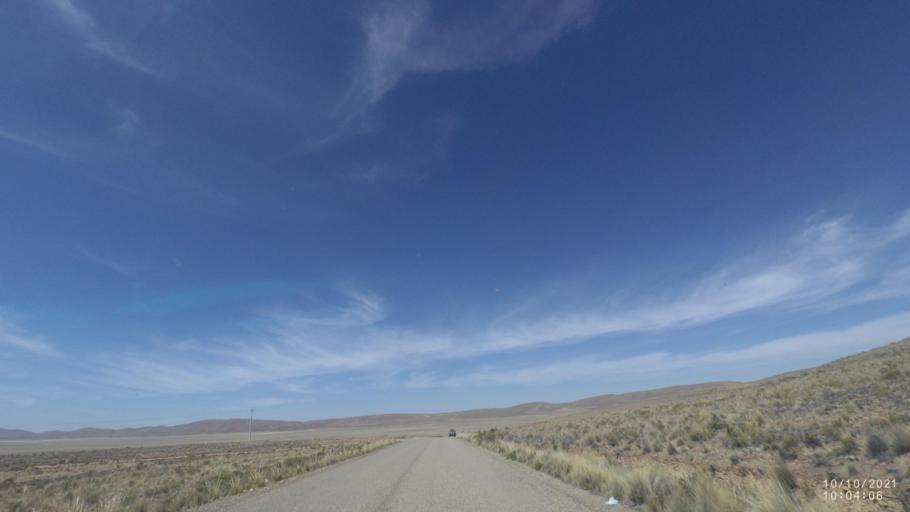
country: BO
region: La Paz
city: Eucaliptus
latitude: -17.3791
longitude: -67.4423
